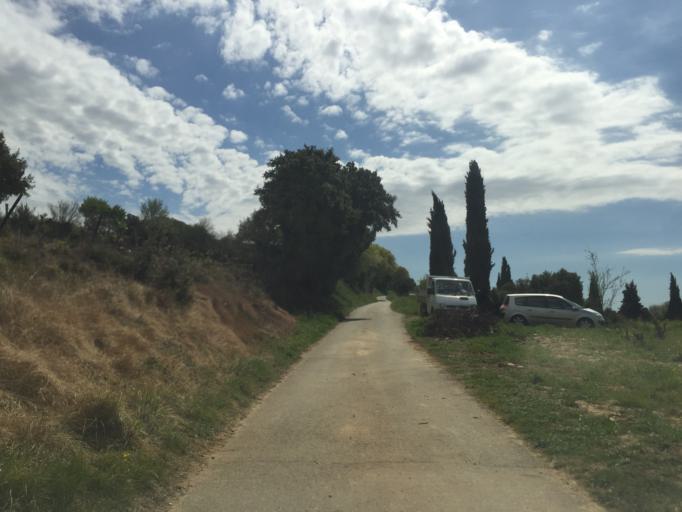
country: FR
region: Provence-Alpes-Cote d'Azur
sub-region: Departement du Vaucluse
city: Chateauneuf-du-Pape
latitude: 44.0644
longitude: 4.8228
